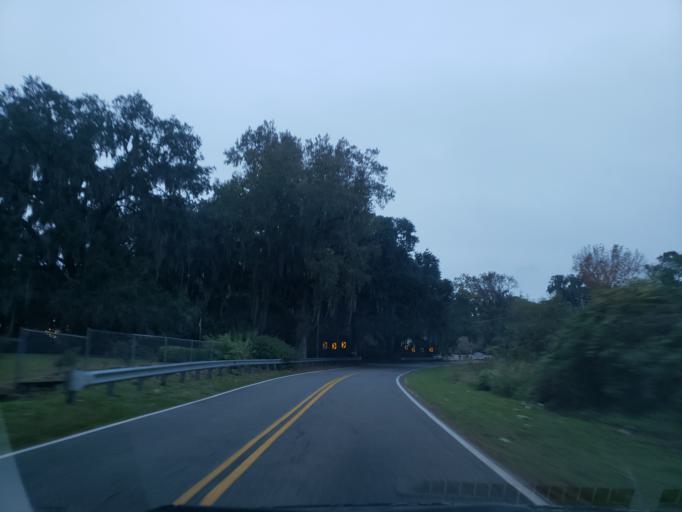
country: US
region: Georgia
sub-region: Chatham County
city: Isle of Hope
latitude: 32.0084
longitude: -81.0659
